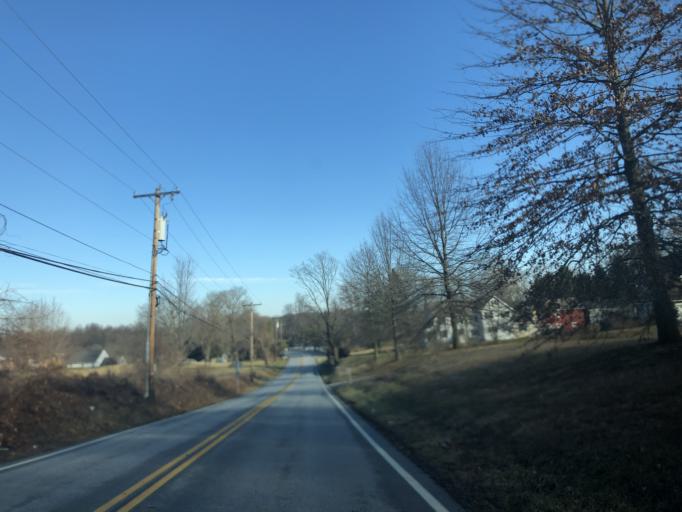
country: US
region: Pennsylvania
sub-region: Delaware County
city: Chester Heights
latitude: 39.8696
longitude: -75.4684
